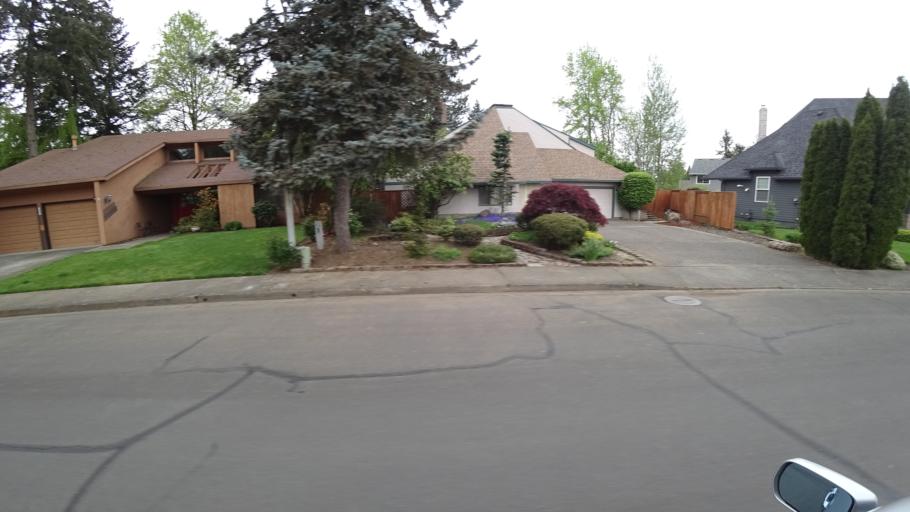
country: US
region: Oregon
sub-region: Washington County
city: Hillsboro
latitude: 45.5368
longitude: -122.9833
